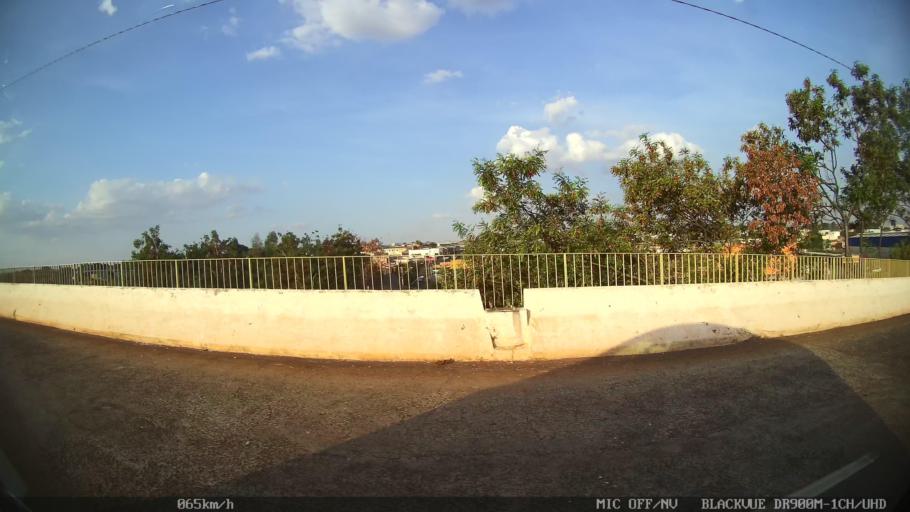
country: BR
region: Sao Paulo
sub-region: Ribeirao Preto
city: Ribeirao Preto
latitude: -21.1376
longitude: -47.8032
